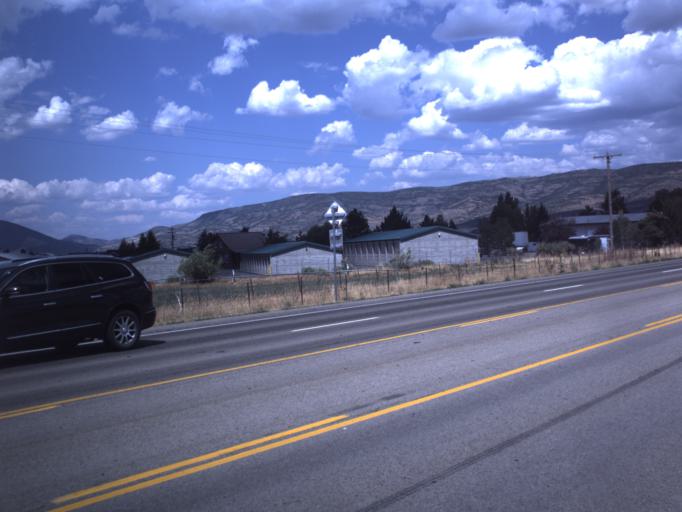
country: US
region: Utah
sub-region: Wasatch County
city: Heber
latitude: 40.4882
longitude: -111.4207
